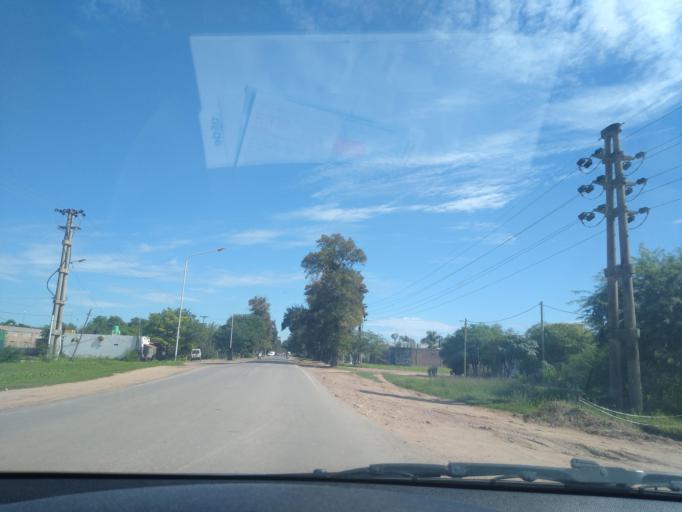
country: AR
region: Chaco
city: Presidencia Roque Saenz Pena
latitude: -26.7721
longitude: -60.4205
